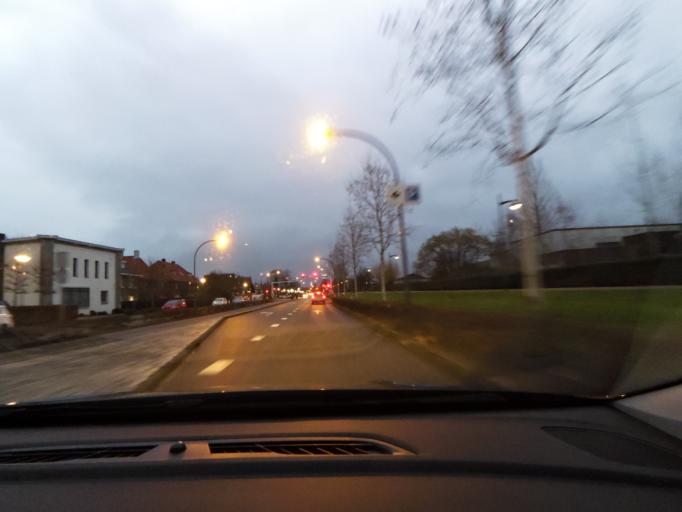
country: NL
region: North Brabant
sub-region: Gemeente Waalwijk
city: Waalwijk
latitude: 51.6848
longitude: 5.0688
